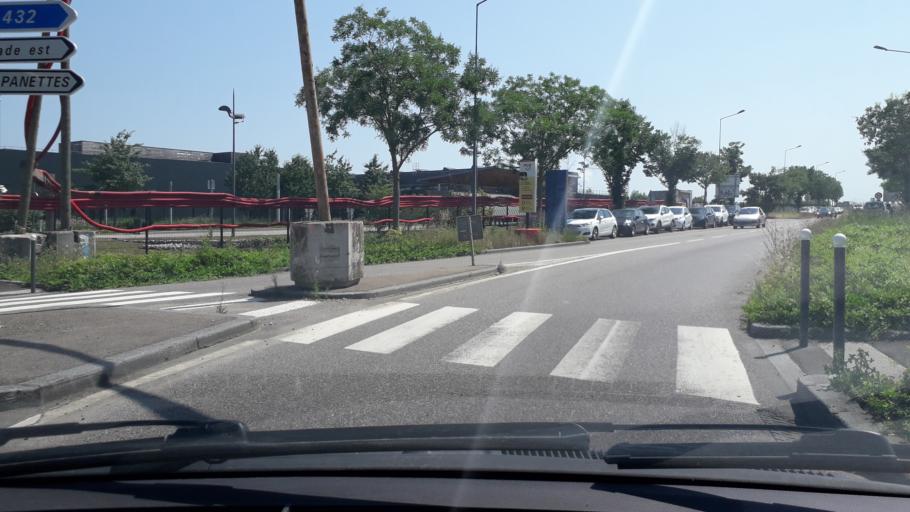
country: FR
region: Rhone-Alpes
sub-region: Departement du Rhone
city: Jonage
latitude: 45.7694
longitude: 5.0357
